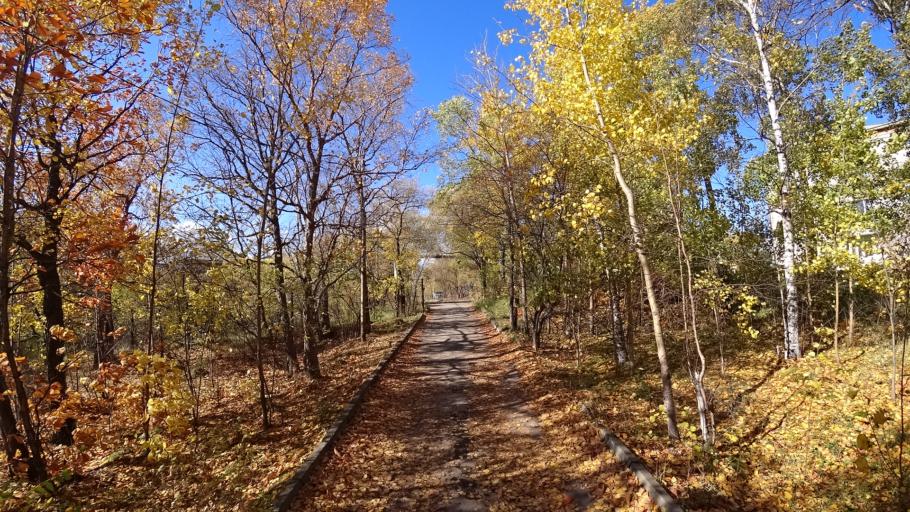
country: RU
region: Khabarovsk Krai
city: Amursk
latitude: 50.2191
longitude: 136.9064
